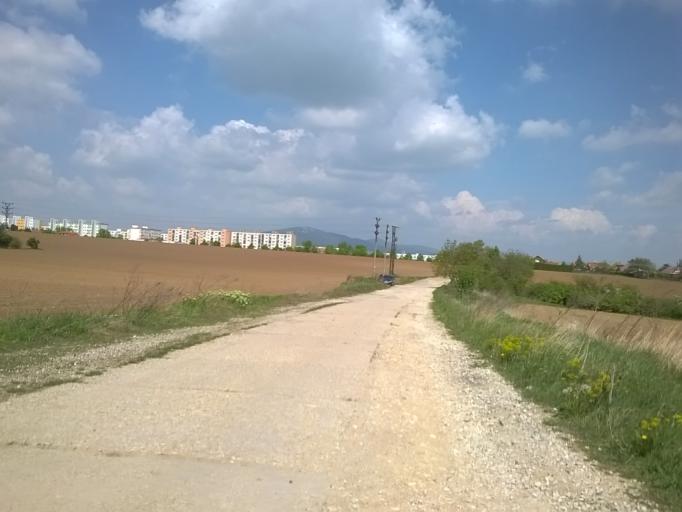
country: SK
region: Nitriansky
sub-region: Okres Nitra
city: Nitra
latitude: 48.2910
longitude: 18.0556
